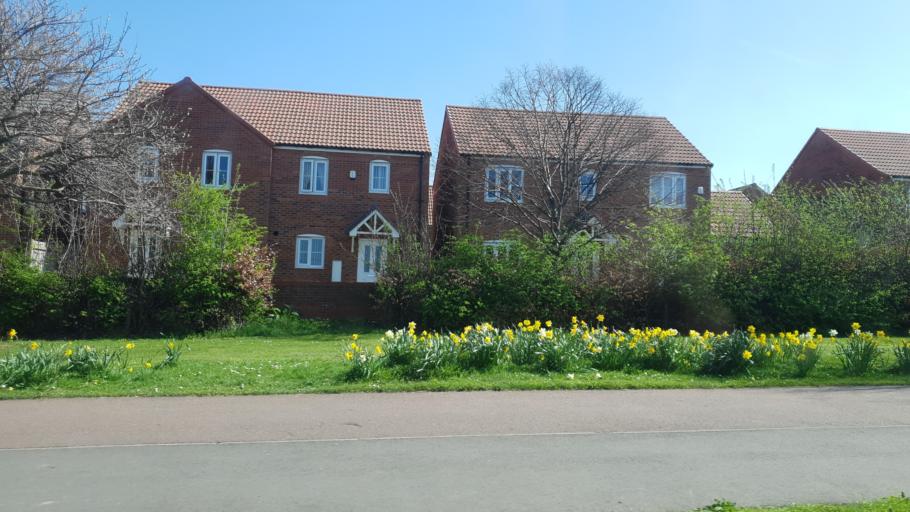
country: GB
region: England
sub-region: Middlesbrough
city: Middlesbrough
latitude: 54.5479
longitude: -1.2163
